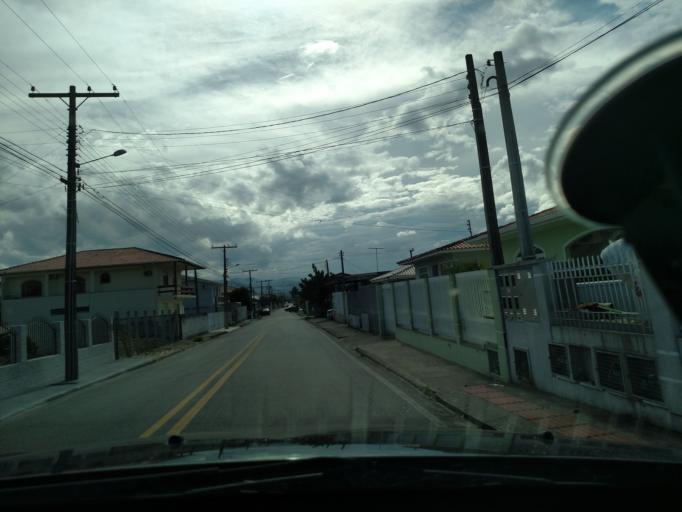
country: BR
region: Santa Catarina
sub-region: Sao Jose
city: Campinas
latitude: -27.6043
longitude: -48.6443
